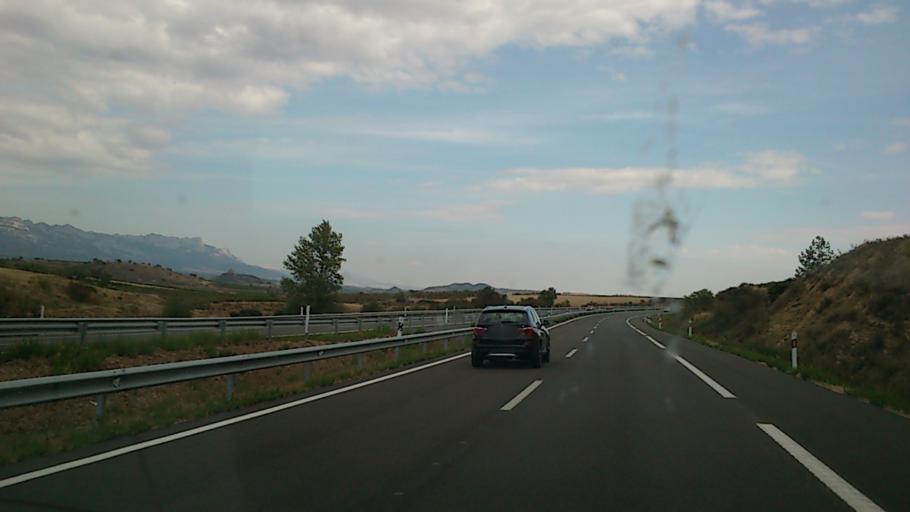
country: ES
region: La Rioja
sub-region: Provincia de La Rioja
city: Briones
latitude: 42.5231
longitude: -2.7747
